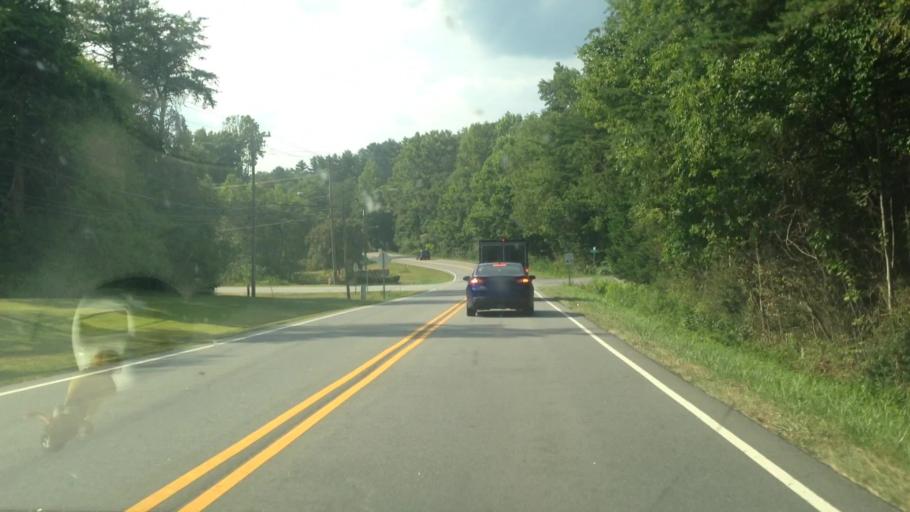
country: US
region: North Carolina
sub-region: Forsyth County
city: Kernersville
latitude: 36.1253
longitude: -80.1121
